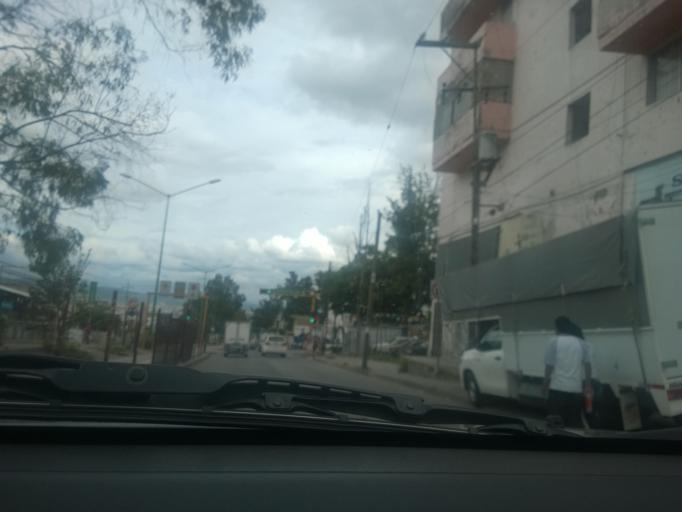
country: MX
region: Guanajuato
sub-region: Leon
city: La Ermita
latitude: 21.1316
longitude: -101.7080
